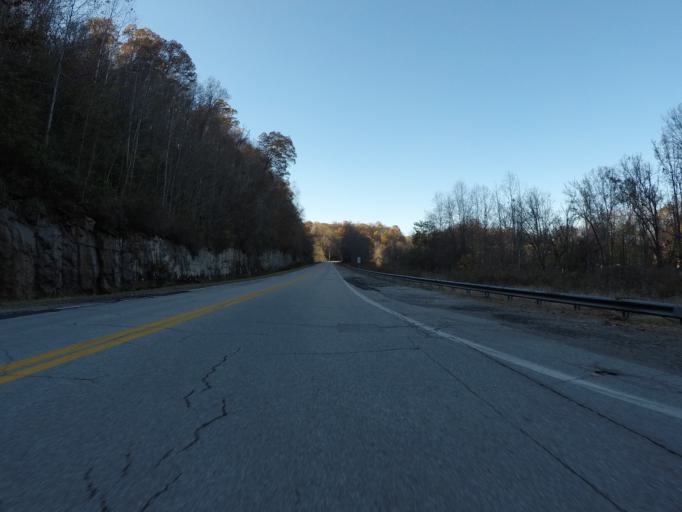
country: US
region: West Virginia
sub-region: Wayne County
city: Ceredo
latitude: 38.3766
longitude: -82.5593
